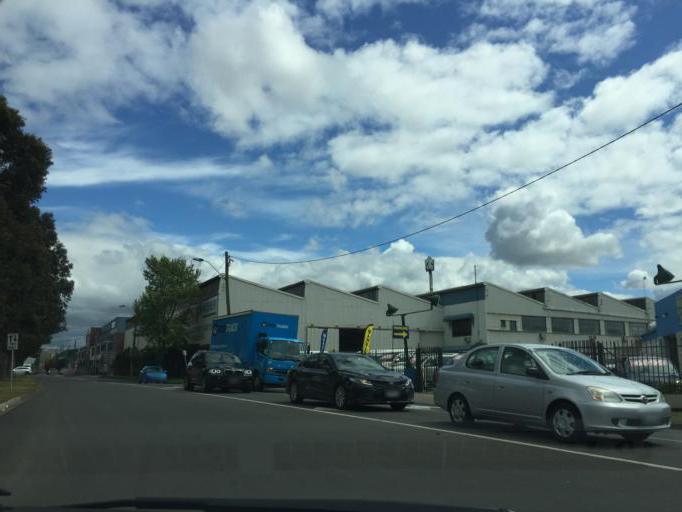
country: AU
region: Victoria
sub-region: Maribyrnong
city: Braybrook
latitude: -37.7928
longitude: 144.8630
